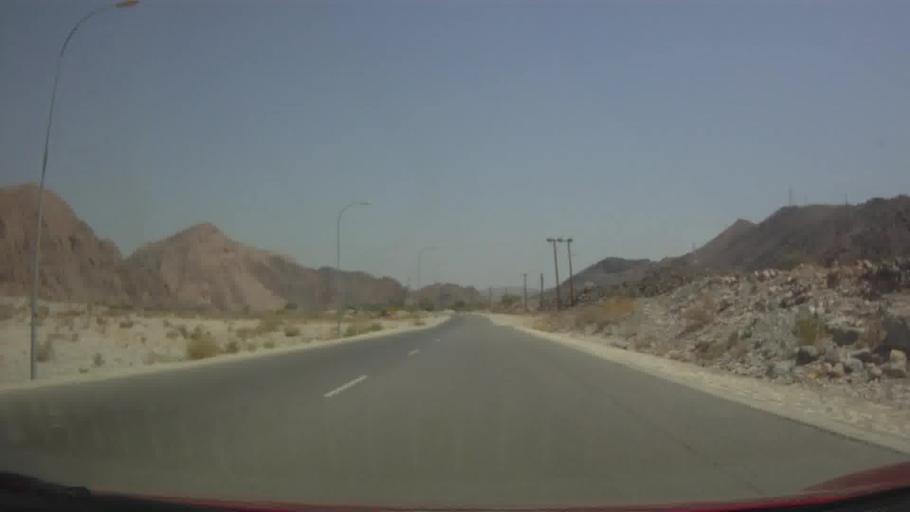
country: OM
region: Muhafazat Masqat
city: Muscat
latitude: 23.5098
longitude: 58.6369
